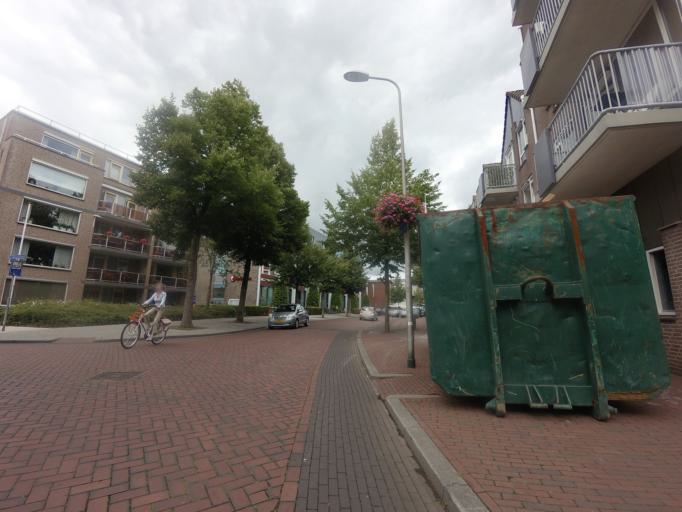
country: NL
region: Drenthe
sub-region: Gemeente Meppel
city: Meppel
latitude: 52.6978
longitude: 6.1881
